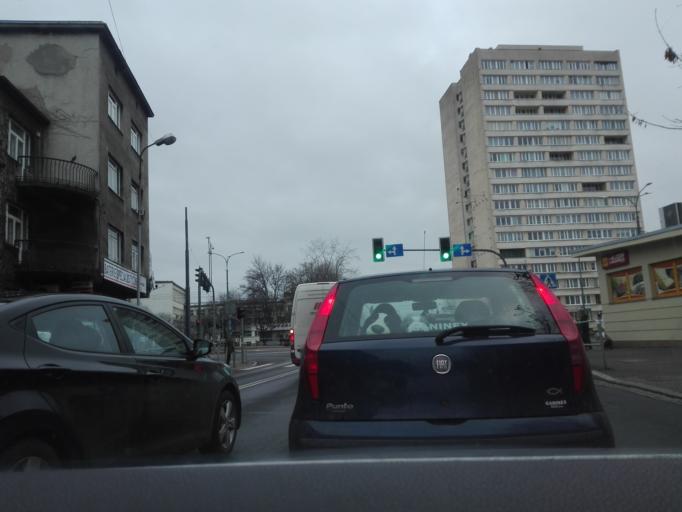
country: PL
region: Silesian Voivodeship
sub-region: Katowice
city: Katowice
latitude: 50.2705
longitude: 19.0237
